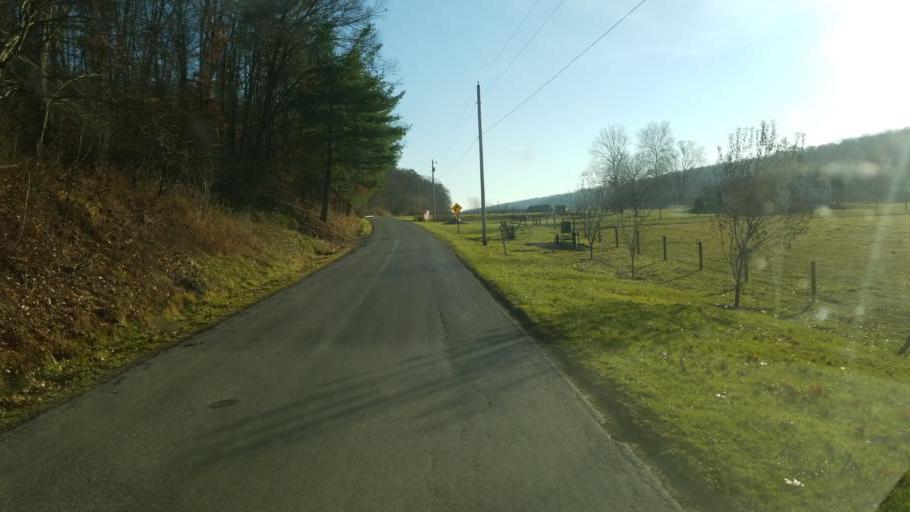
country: US
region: Ohio
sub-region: Wayne County
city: West Salem
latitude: 40.9056
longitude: -82.0068
